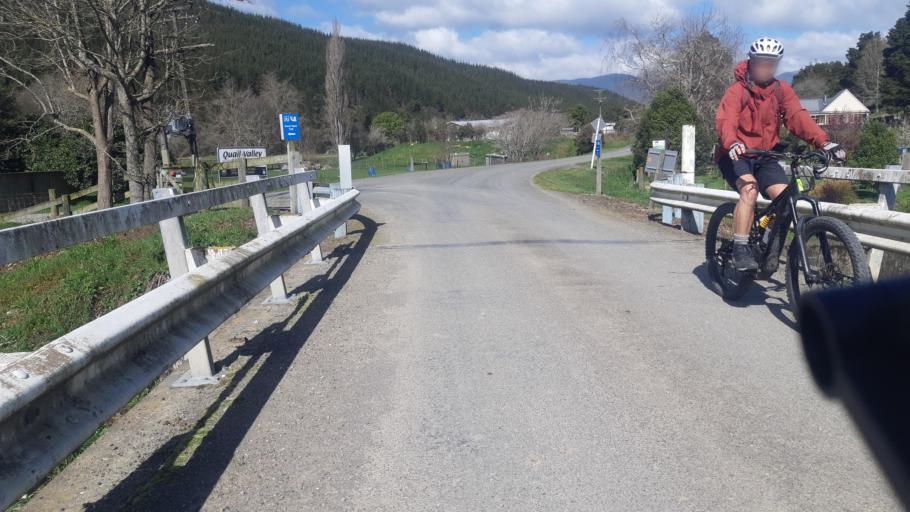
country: NZ
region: Tasman
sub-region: Tasman District
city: Wakefield
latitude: -41.4484
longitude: 172.9669
